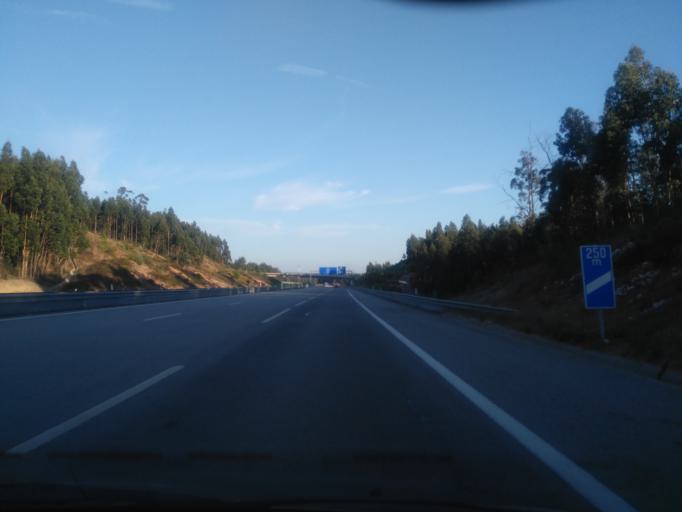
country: PT
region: Coimbra
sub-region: Figueira da Foz
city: Alhadas
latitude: 40.1640
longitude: -8.7818
